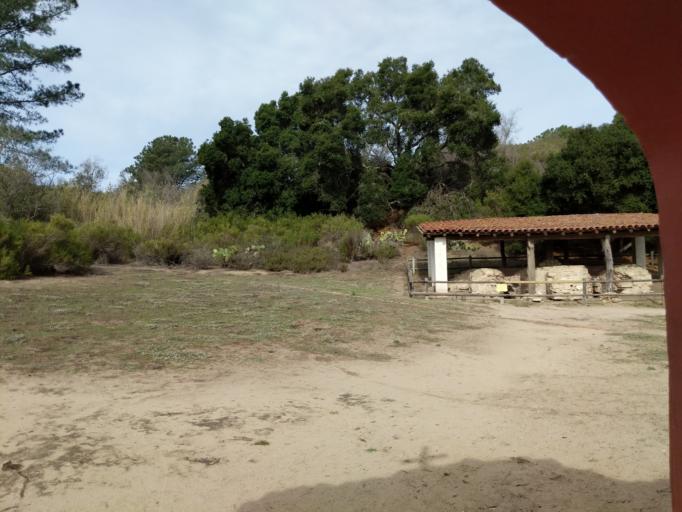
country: US
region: California
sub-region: Santa Barbara County
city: Mission Hills
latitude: 34.6716
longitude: -120.4228
